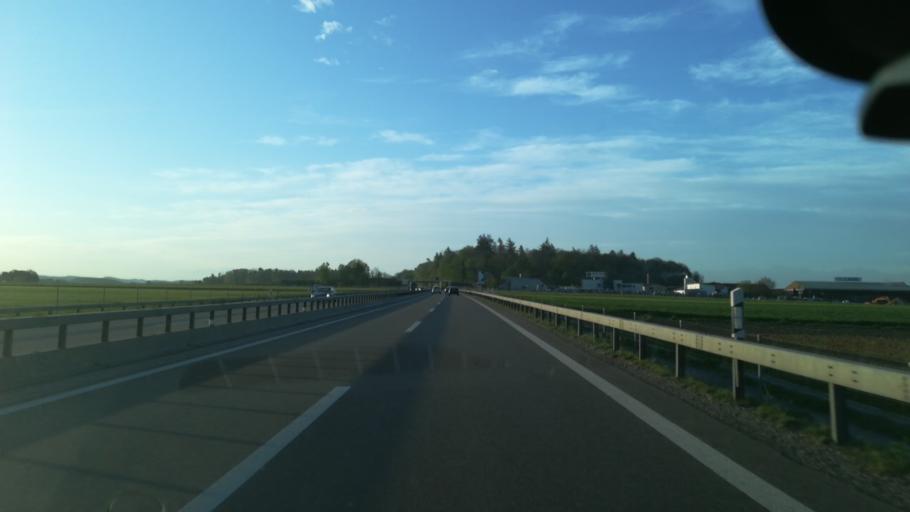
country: CH
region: Zurich
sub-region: Bezirk Andelfingen
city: Marthalen
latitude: 47.6388
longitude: 8.6581
